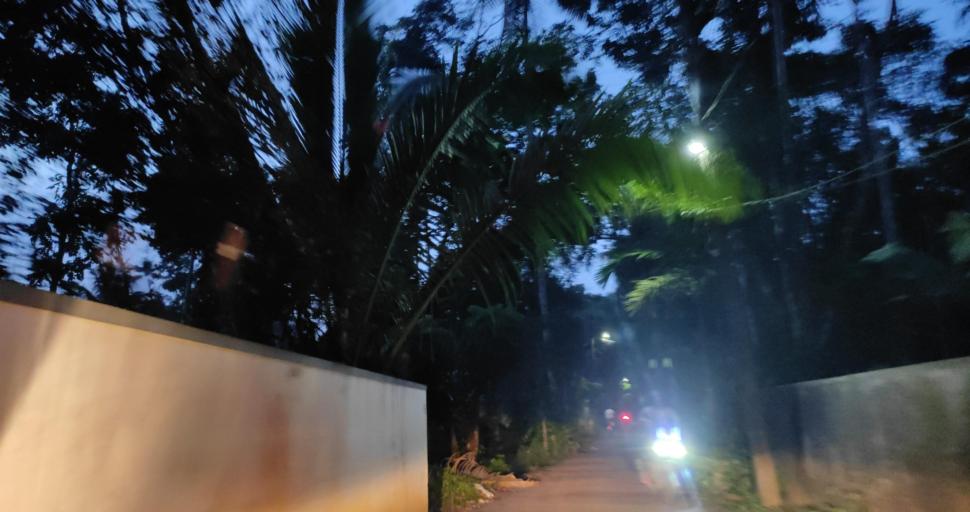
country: IN
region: Kerala
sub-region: Alappuzha
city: Vayalar
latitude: 9.7219
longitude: 76.2913
